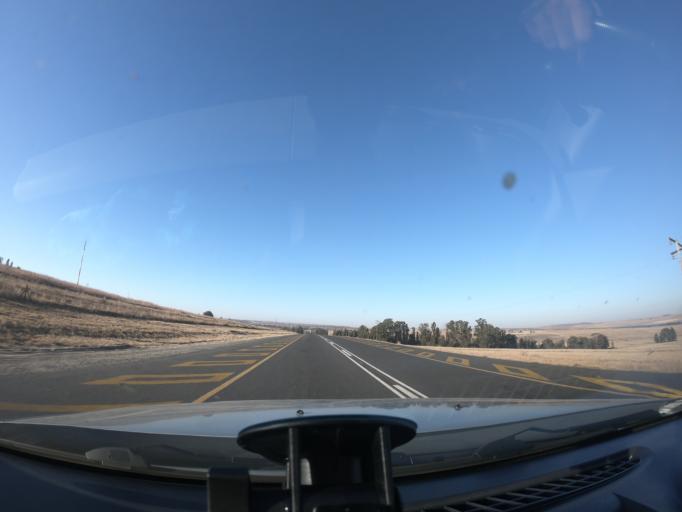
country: ZA
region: Mpumalanga
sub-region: Gert Sibande District Municipality
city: Ermelo
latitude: -26.4415
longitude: 29.9474
